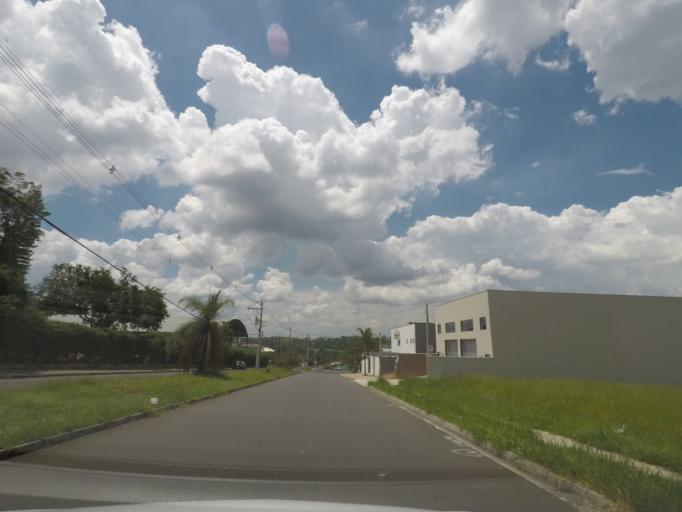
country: BR
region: Sao Paulo
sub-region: Valinhos
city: Valinhos
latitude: -22.9445
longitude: -46.9936
